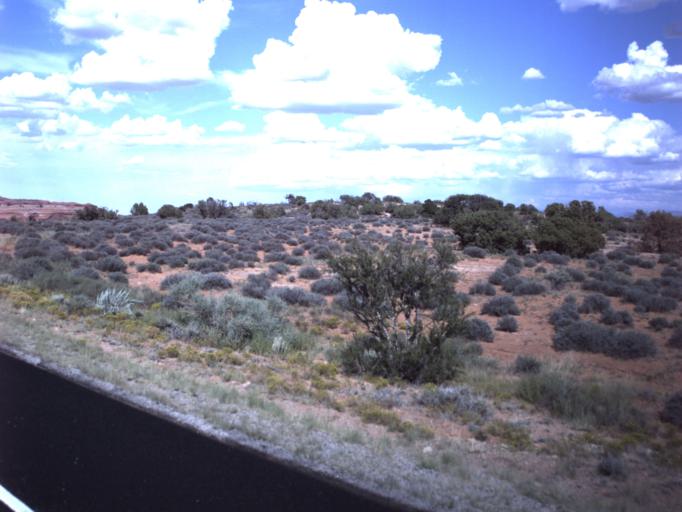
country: US
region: Utah
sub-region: Grand County
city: Moab
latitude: 38.6252
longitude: -109.8095
